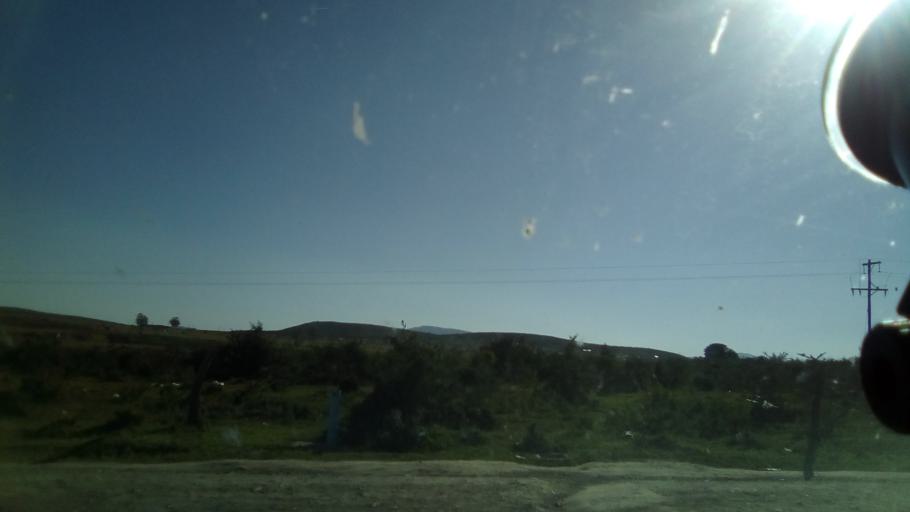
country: ZA
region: Eastern Cape
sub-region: Buffalo City Metropolitan Municipality
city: Bhisho
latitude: -32.8247
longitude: 27.3686
